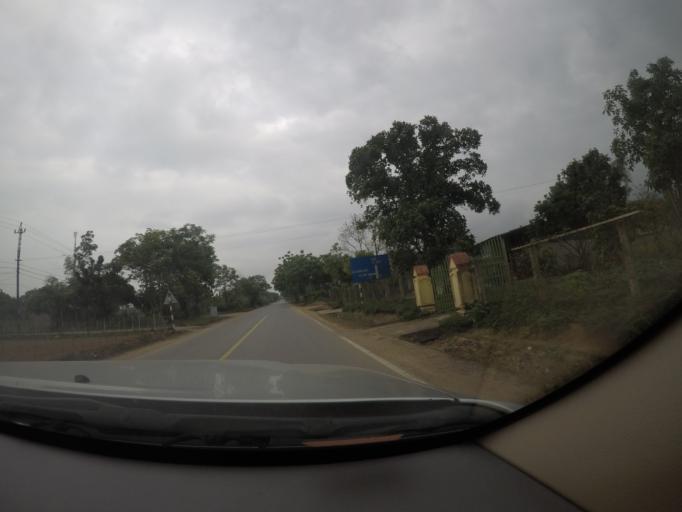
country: VN
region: Quang Binh
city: Hoan Lao
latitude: 17.5832
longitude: 106.4344
